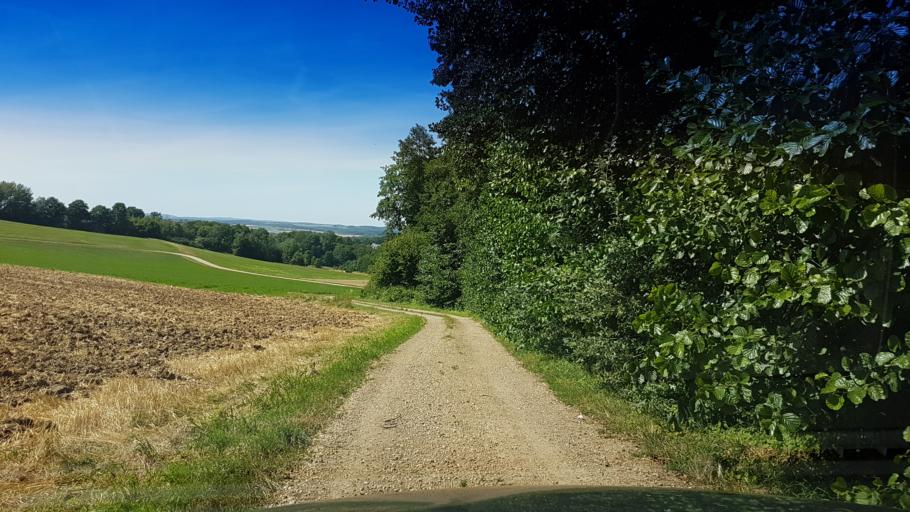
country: DE
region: Bavaria
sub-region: Upper Franconia
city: Schesslitz
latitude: 49.9430
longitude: 11.0522
